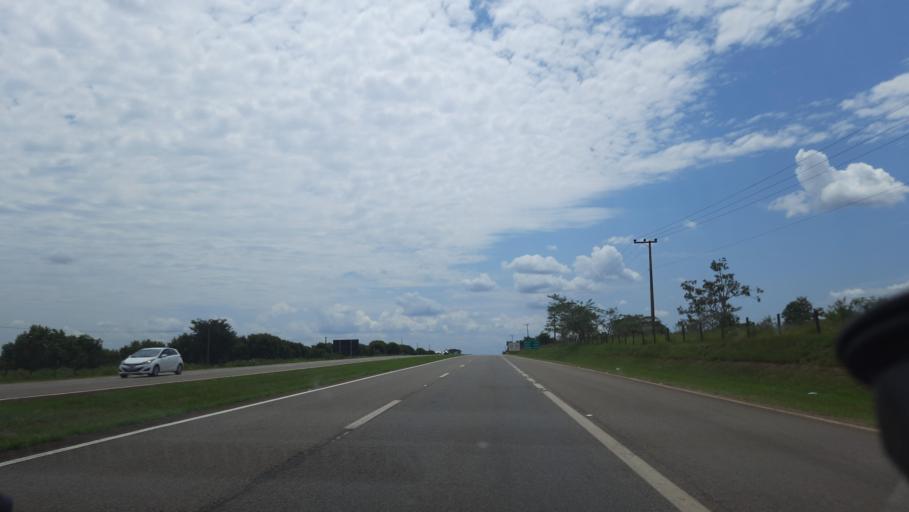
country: BR
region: Sao Paulo
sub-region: Casa Branca
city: Casa Branca
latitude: -21.7471
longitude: -47.0721
